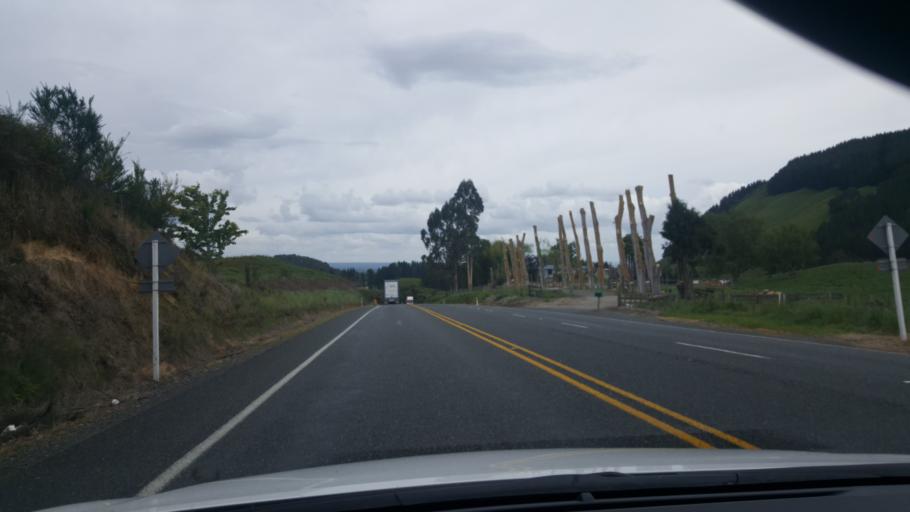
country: NZ
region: Bay of Plenty
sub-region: Rotorua District
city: Rotorua
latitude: -38.3486
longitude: 176.3612
